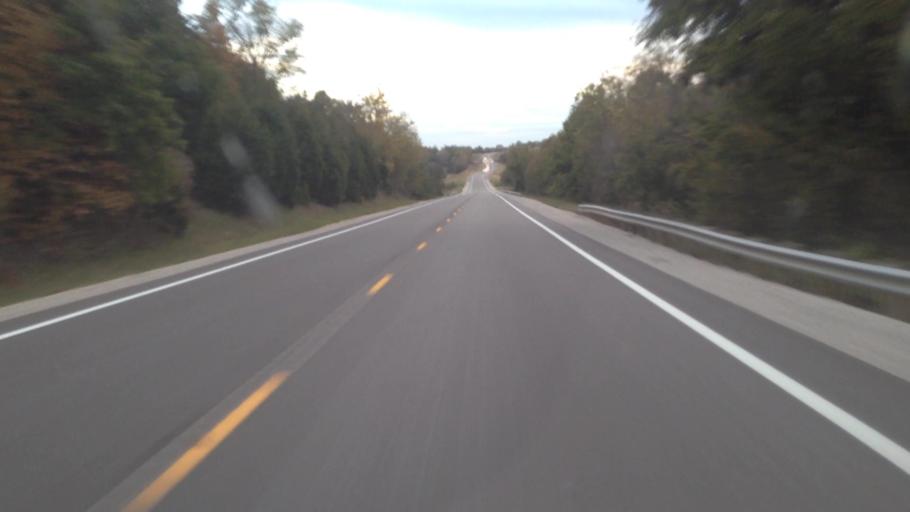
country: US
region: Kansas
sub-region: Anderson County
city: Garnett
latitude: 38.3455
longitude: -95.2488
